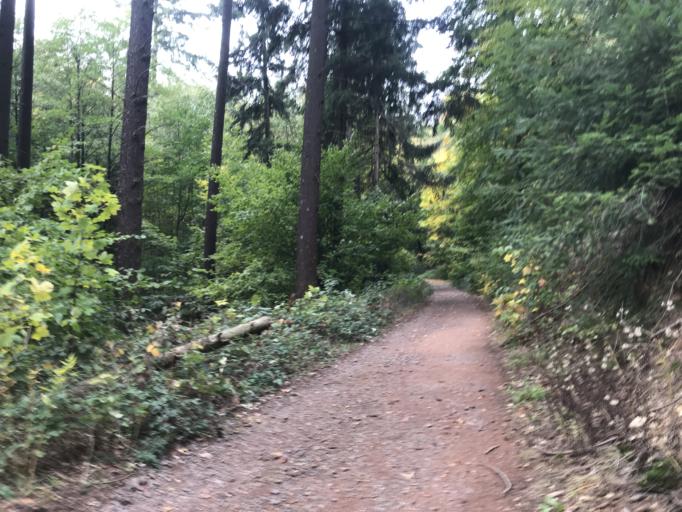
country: DE
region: Rheinland-Pfalz
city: Kirchheimbolanden
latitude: 49.6549
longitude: 7.9942
